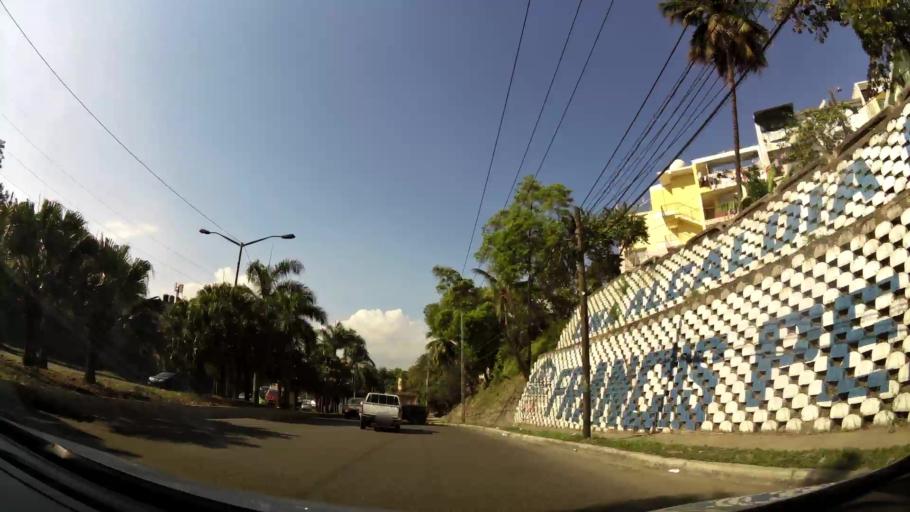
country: DO
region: Santo Domingo
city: Santo Domingo Oeste
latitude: 18.4723
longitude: -69.9941
